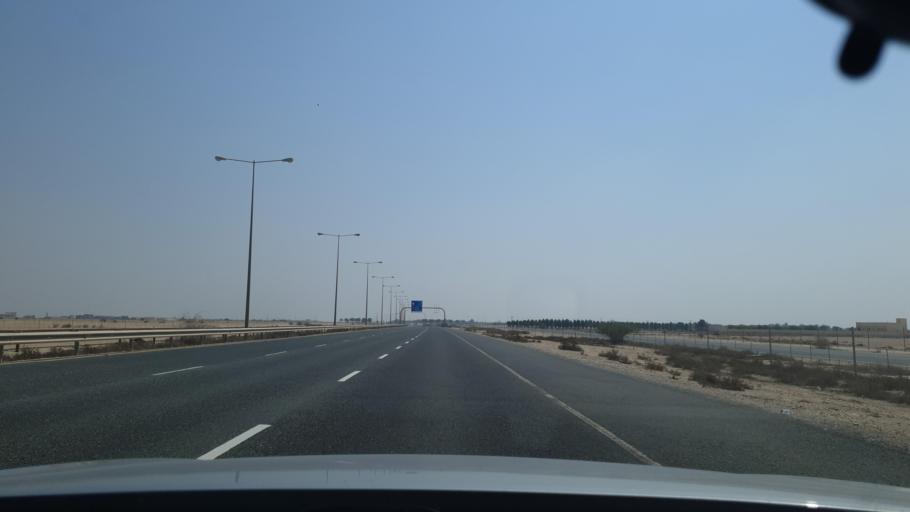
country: QA
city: Al Ghuwayriyah
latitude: 25.7943
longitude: 51.3880
